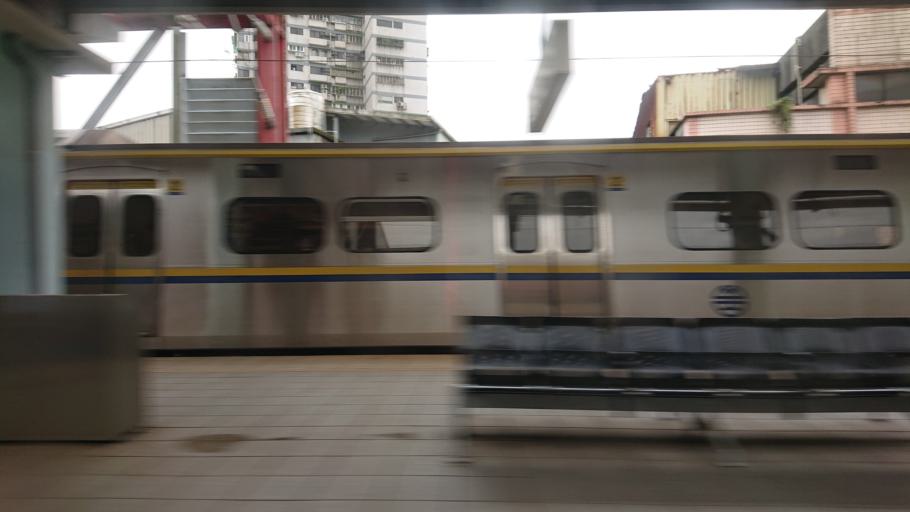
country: TW
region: Taiwan
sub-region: Keelung
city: Keelung
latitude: 25.0777
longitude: 121.6673
